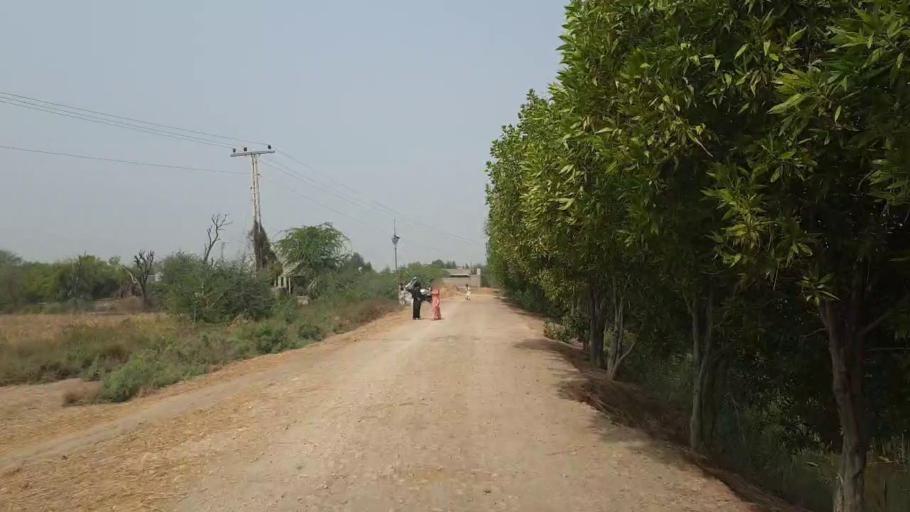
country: PK
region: Sindh
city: Kario
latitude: 24.6577
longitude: 68.6390
